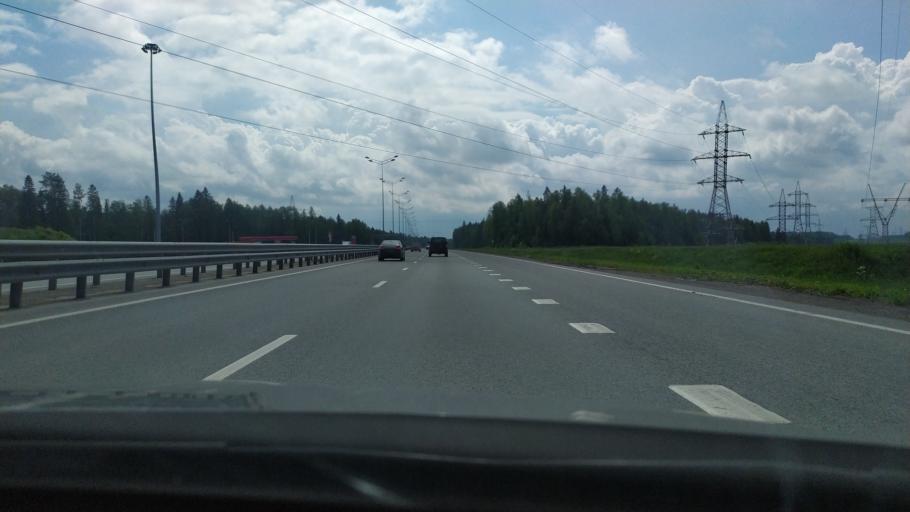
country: RU
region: Perm
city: Novyye Lyady
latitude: 58.0434
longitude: 56.4308
